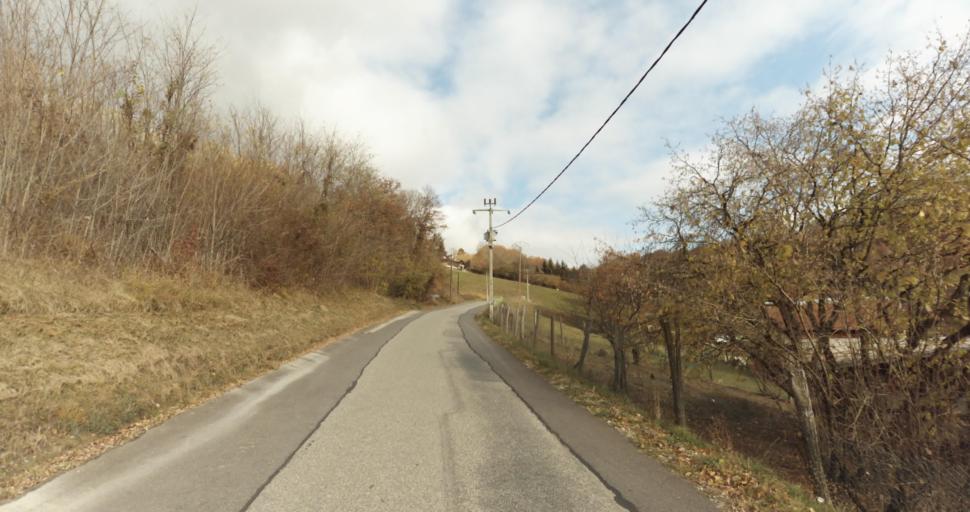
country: FR
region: Rhone-Alpes
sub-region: Departement de la Haute-Savoie
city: Epagny
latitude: 45.9500
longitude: 6.0773
